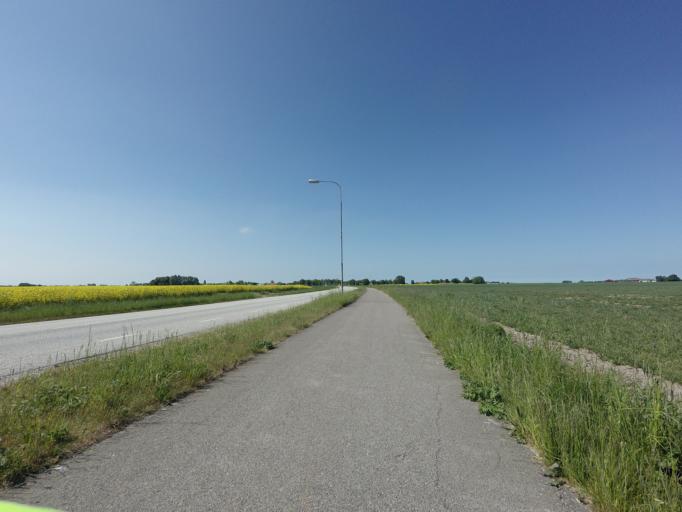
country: SE
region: Skane
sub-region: Vellinge Kommun
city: Vellinge
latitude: 55.4660
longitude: 13.0054
